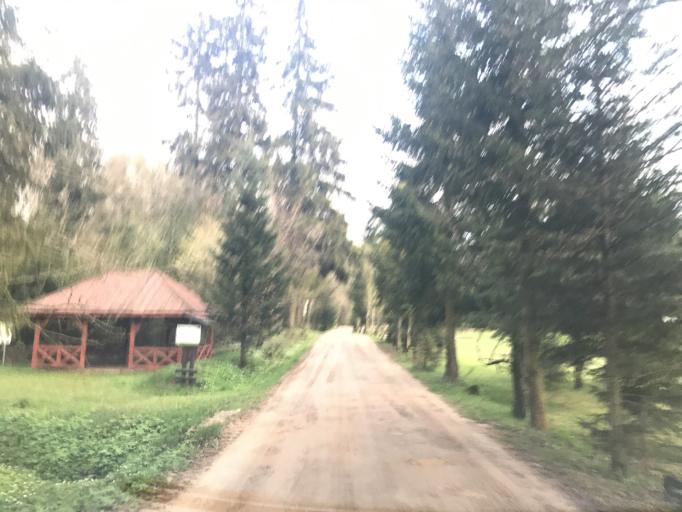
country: PL
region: Warmian-Masurian Voivodeship
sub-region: Powiat dzialdowski
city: Rybno
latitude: 53.5115
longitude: 19.8989
